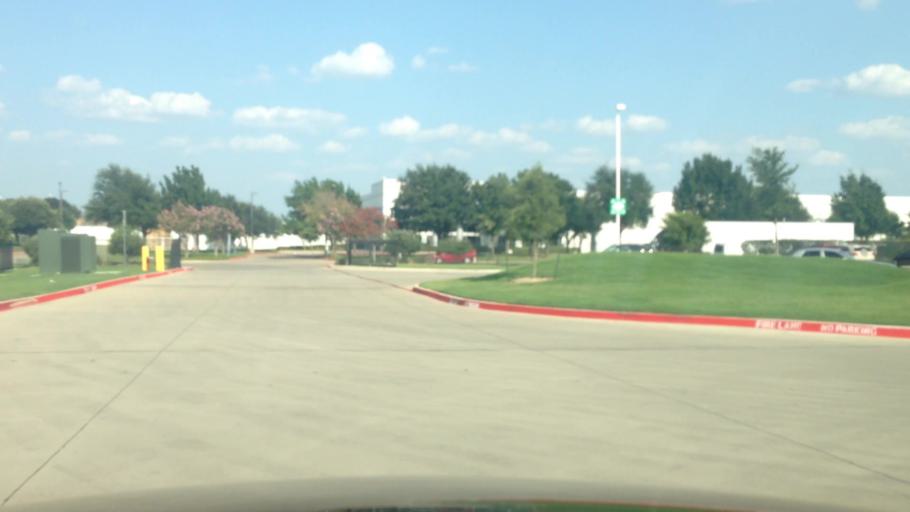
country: US
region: Texas
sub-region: Tarrant County
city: Blue Mound
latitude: 32.8296
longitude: -97.3534
